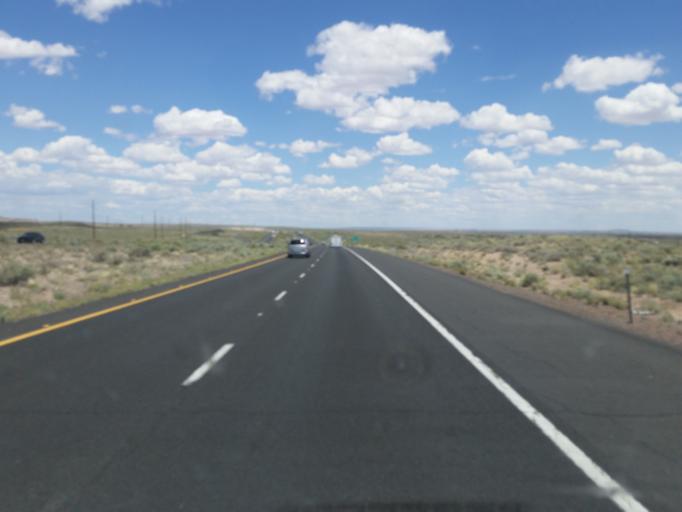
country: US
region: Arizona
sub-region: Navajo County
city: Holbrook
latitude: 34.9906
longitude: -109.9707
